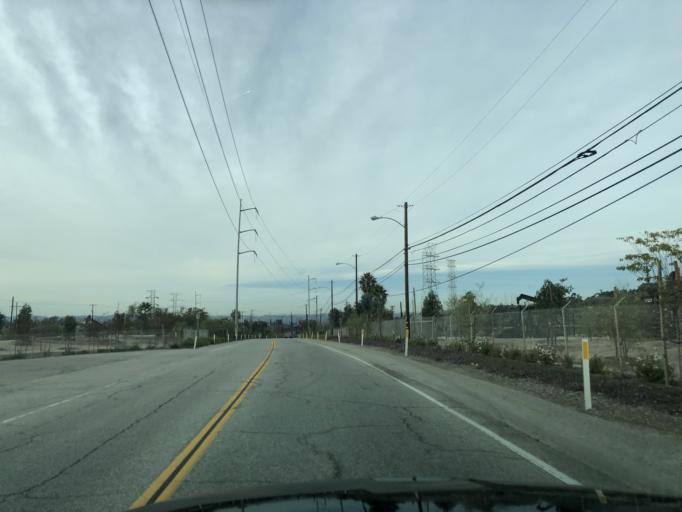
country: US
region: California
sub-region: Los Angeles County
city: Ladera Heights
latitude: 33.9951
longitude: -118.3645
